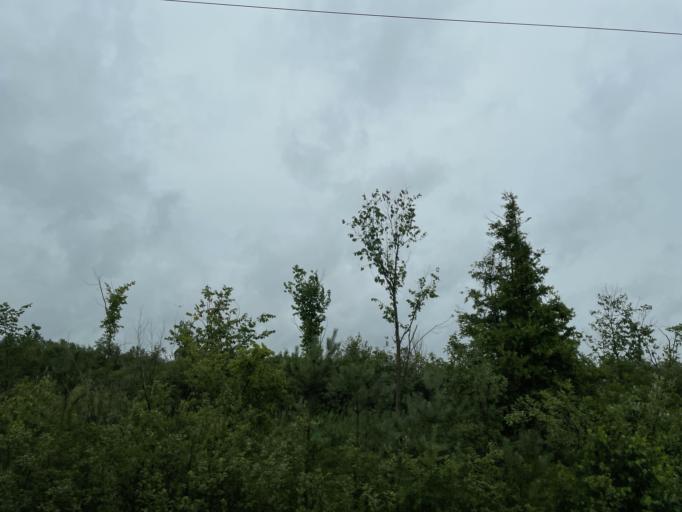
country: CA
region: Ontario
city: Cambridge
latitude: 43.4257
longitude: -80.2592
